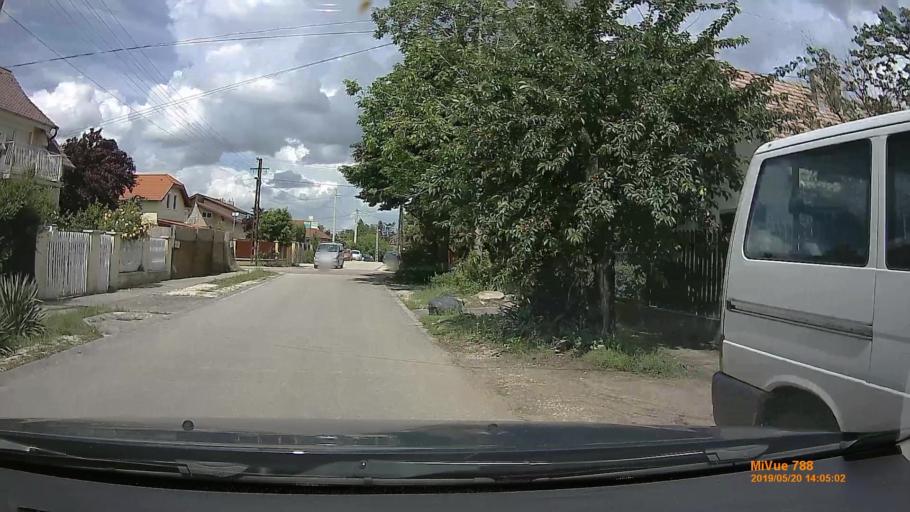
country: HU
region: Budapest
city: Budapest XVII. keruelet
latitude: 47.4726
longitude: 19.2545
